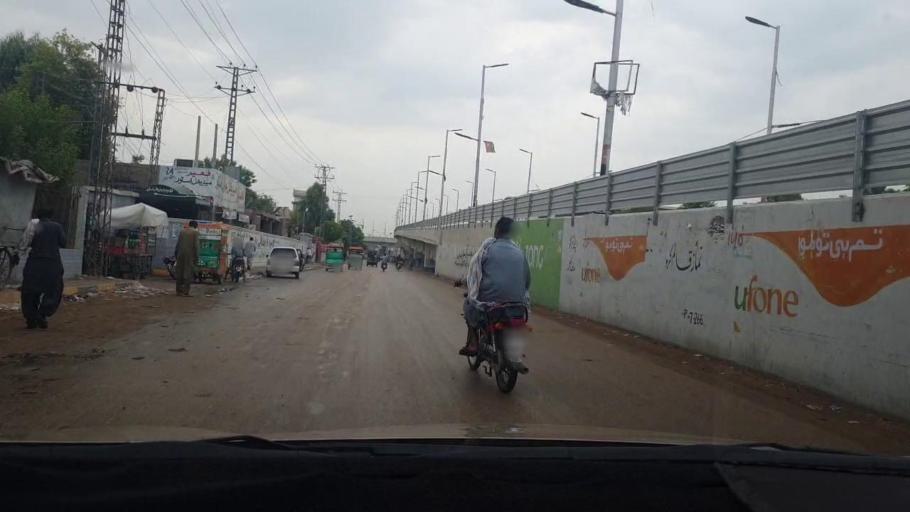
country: PK
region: Sindh
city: Larkana
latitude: 27.5629
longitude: 68.2044
